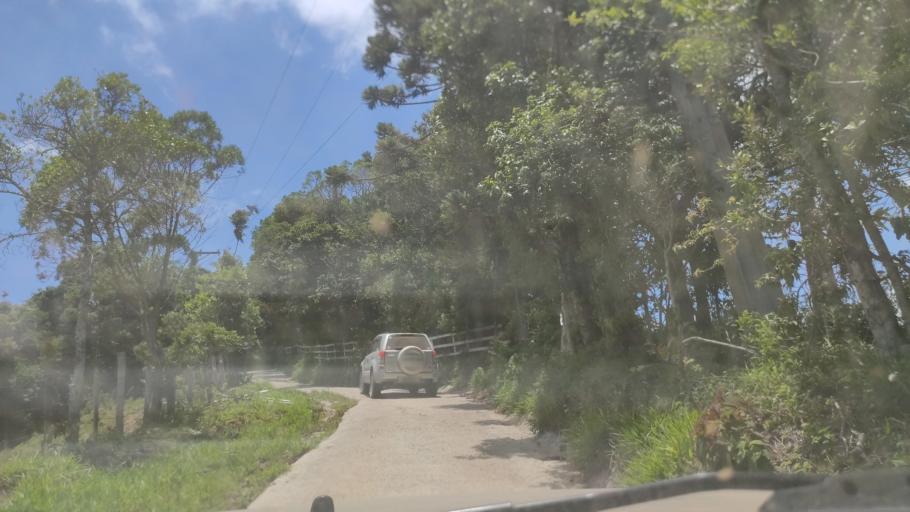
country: BR
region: Minas Gerais
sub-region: Cambui
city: Cambui
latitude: -22.6803
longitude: -45.9680
